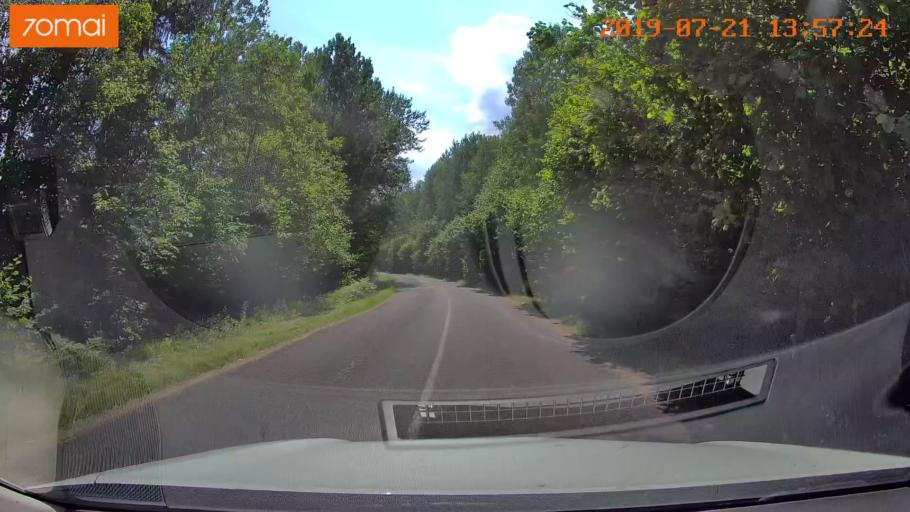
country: BY
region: Grodnenskaya
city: Lyubcha
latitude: 53.7732
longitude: 26.0883
